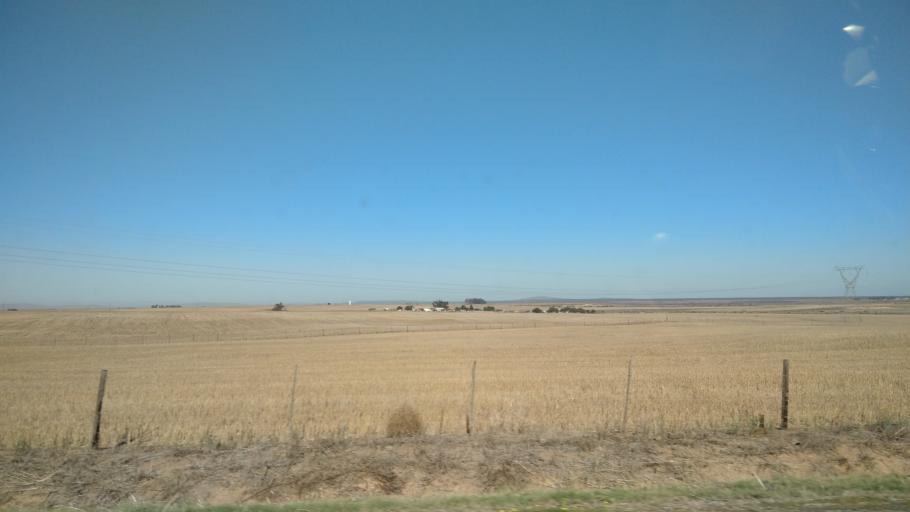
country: ZA
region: Western Cape
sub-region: West Coast District Municipality
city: Moorreesburg
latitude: -33.1551
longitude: 18.4679
